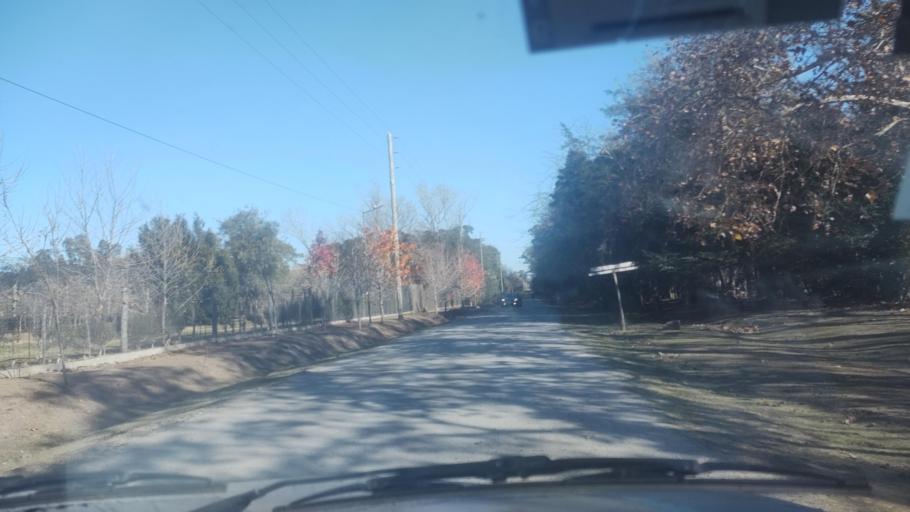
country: AR
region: Buenos Aires
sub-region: Partido de La Plata
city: La Plata
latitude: -34.8559
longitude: -58.1092
